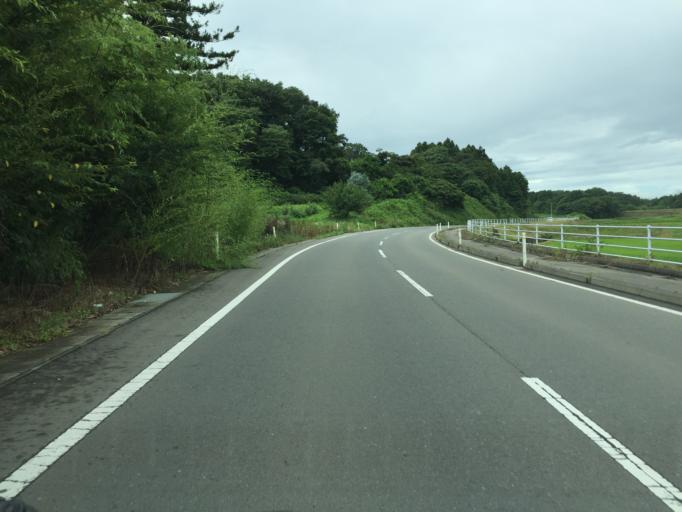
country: JP
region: Miyagi
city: Marumori
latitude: 37.7813
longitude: 140.9537
